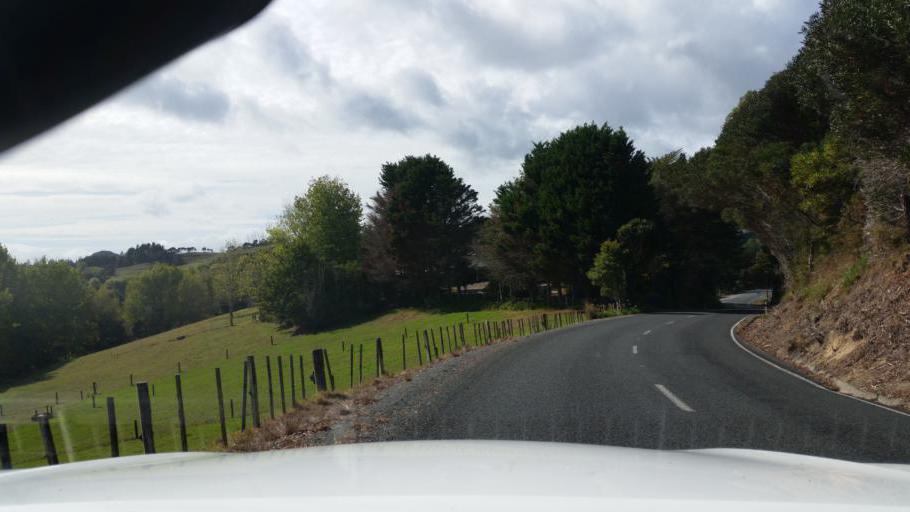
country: NZ
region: Auckland
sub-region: Auckland
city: Wellsford
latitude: -36.0861
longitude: 174.5505
